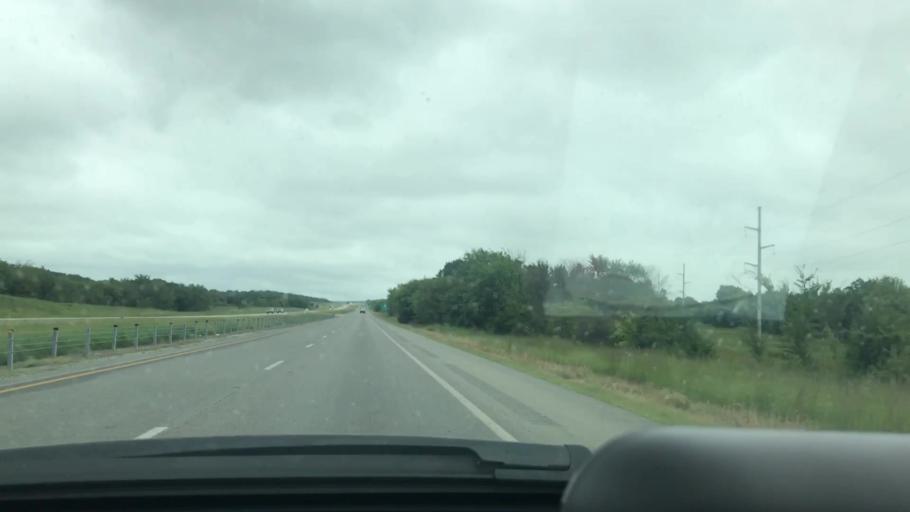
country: US
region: Oklahoma
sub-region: Coal County
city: Coalgate
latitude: 34.6555
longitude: -95.9412
